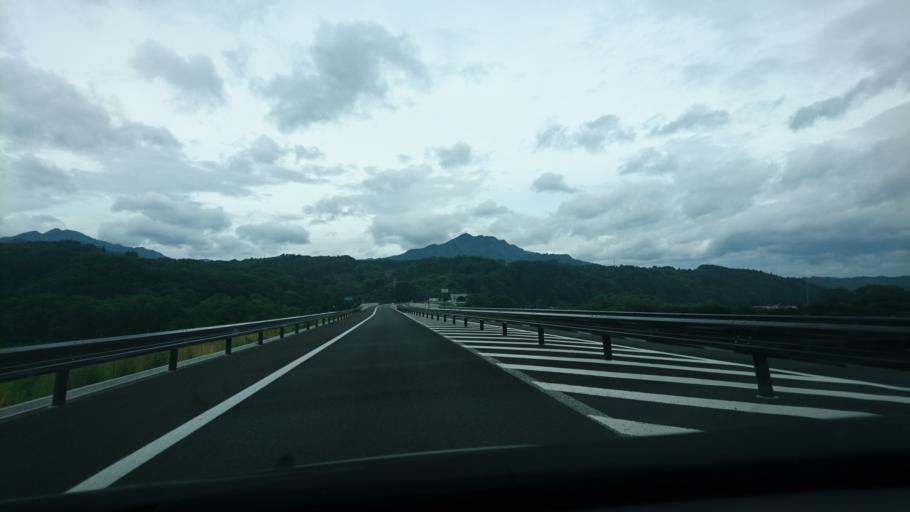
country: JP
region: Iwate
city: Yamada
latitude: 39.5247
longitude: 141.9266
